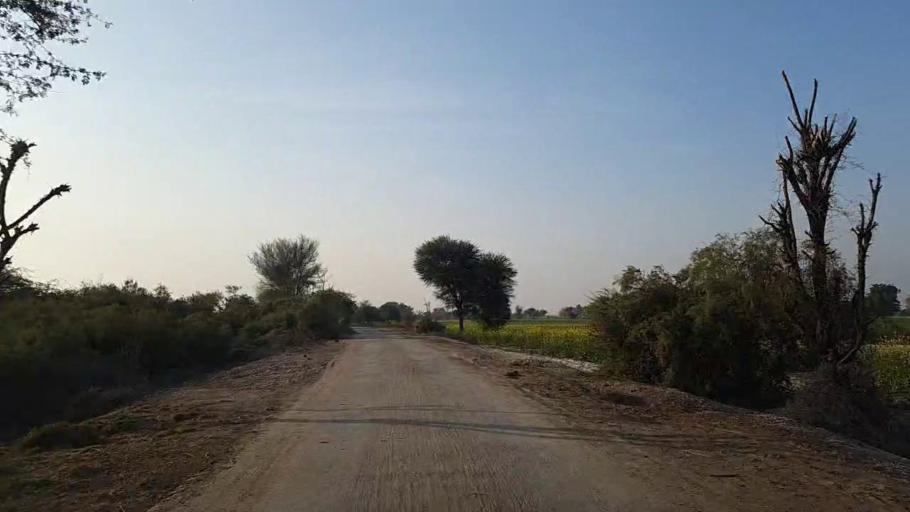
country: PK
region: Sindh
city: Jam Sahib
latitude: 26.3947
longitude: 68.5428
